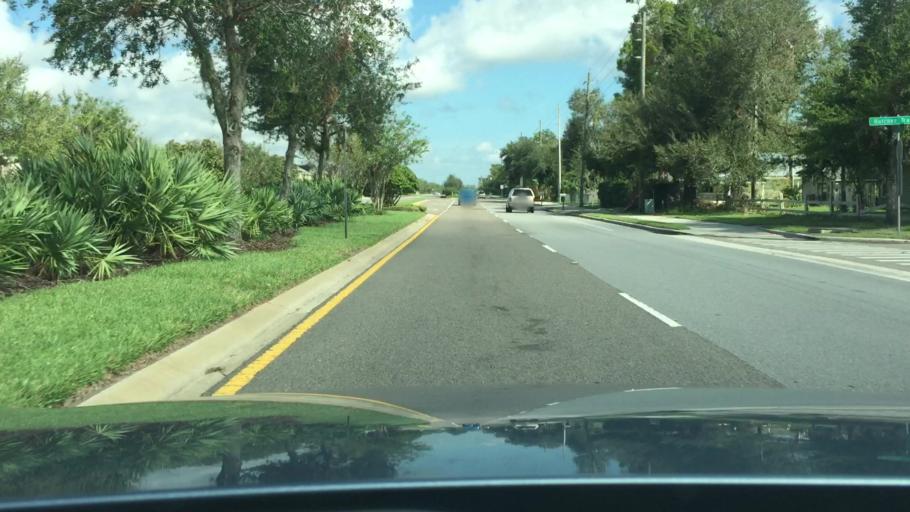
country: US
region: Florida
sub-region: Osceola County
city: Saint Cloud
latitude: 28.2374
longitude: -81.3178
